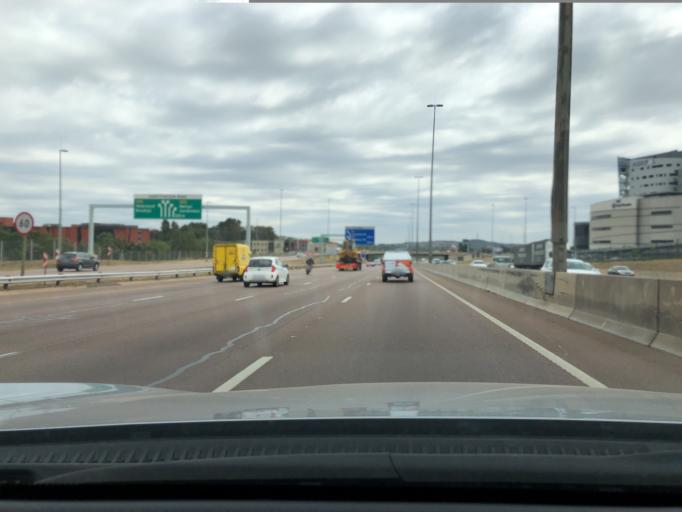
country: ZA
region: Gauteng
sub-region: City of Tshwane Metropolitan Municipality
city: Pretoria
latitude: -25.7882
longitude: 28.2694
